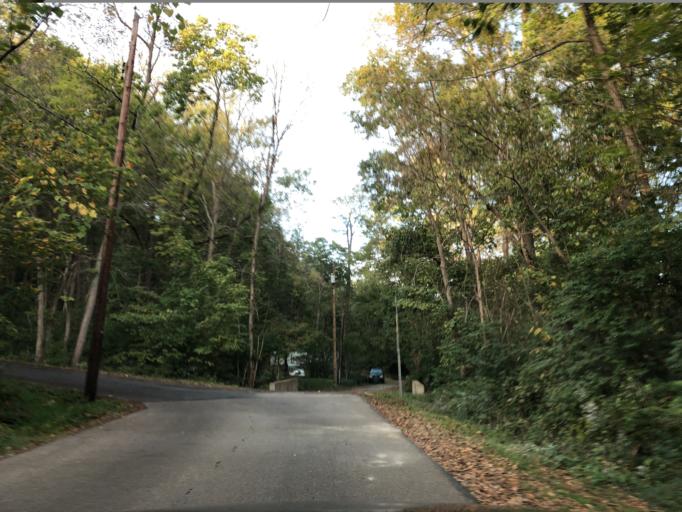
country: US
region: Ohio
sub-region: Warren County
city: Loveland Park
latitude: 39.2849
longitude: -84.2653
